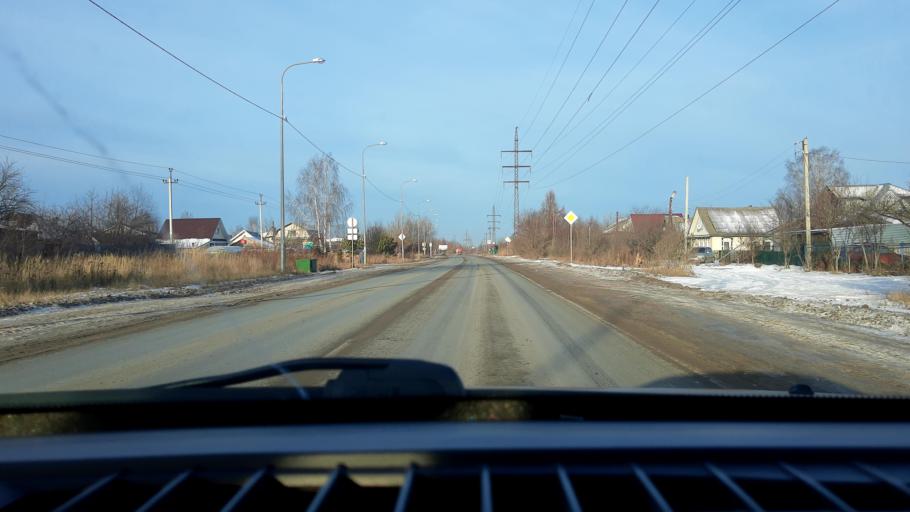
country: RU
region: Nizjnij Novgorod
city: Bor
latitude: 56.3720
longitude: 44.0648
